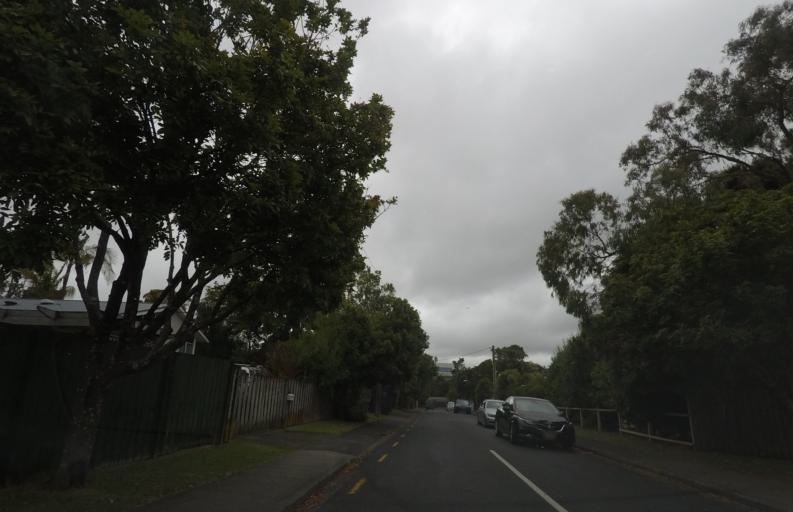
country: NZ
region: Auckland
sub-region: Auckland
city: Rosebank
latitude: -36.8648
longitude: 174.6384
